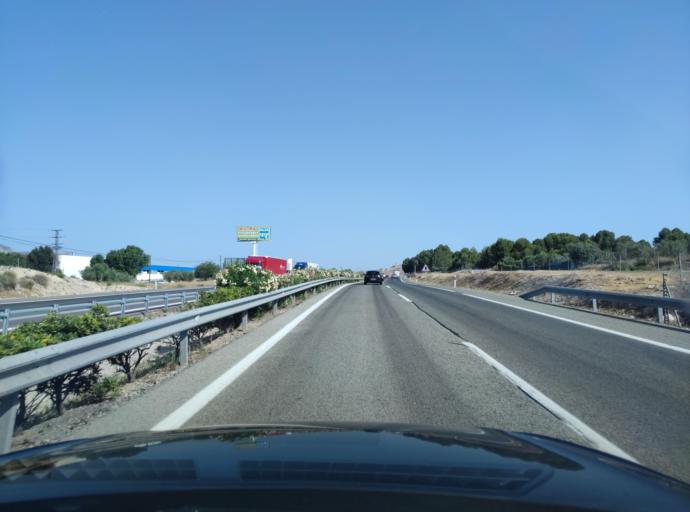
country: ES
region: Valencia
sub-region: Provincia de Alicante
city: Sax
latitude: 38.5236
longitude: -0.8041
